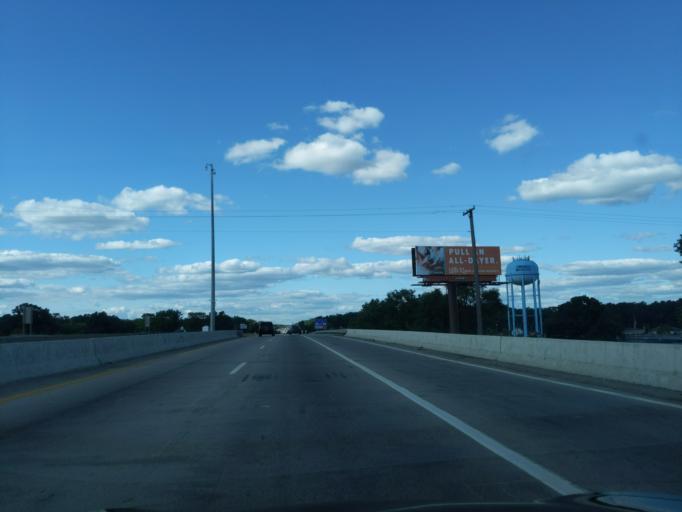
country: US
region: Michigan
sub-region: Muskegon County
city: Muskegon Heights
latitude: 43.2192
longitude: -86.2049
